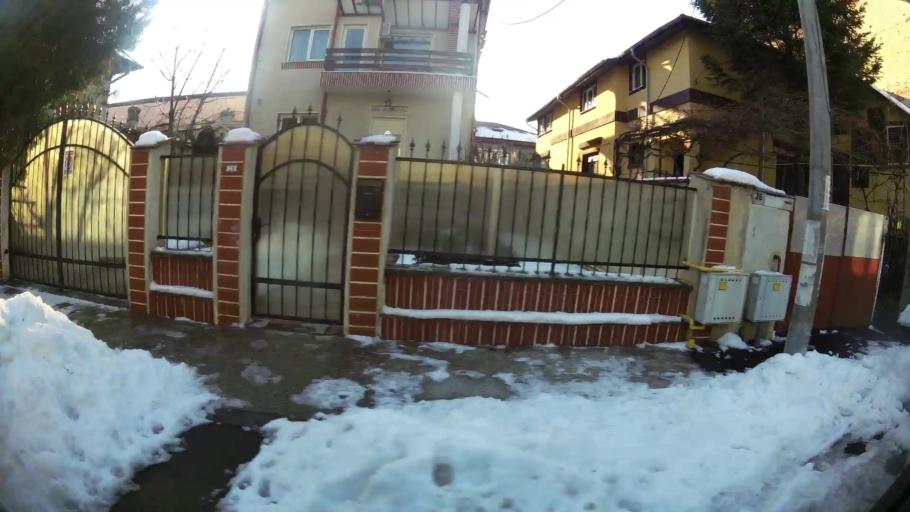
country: RO
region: Bucuresti
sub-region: Municipiul Bucuresti
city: Bucuresti
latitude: 44.4020
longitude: 26.0941
